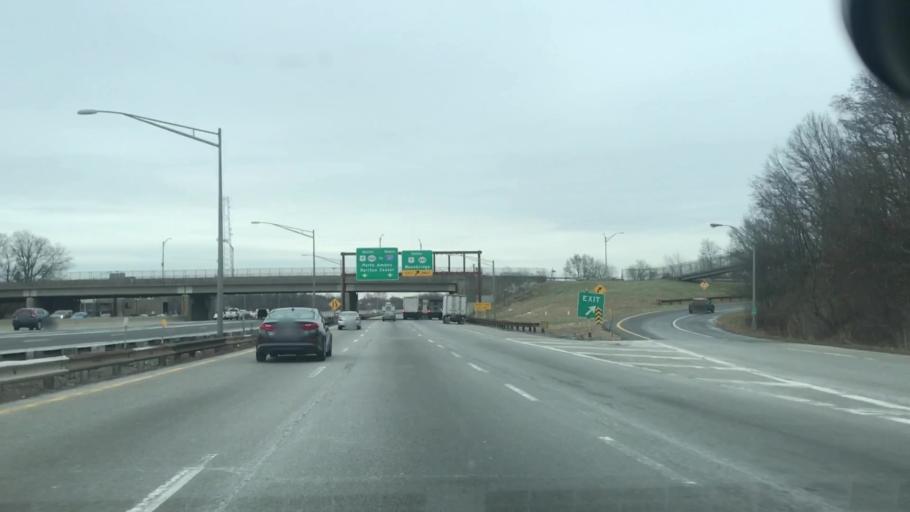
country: US
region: New Jersey
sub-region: Middlesex County
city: Fords
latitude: 40.5351
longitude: -74.3035
